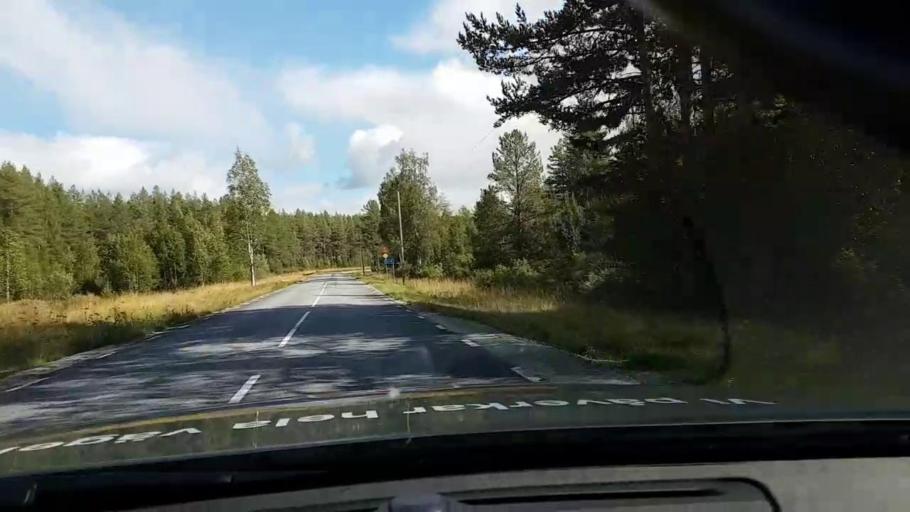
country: SE
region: Vaesterbotten
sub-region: Asele Kommun
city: Asele
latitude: 63.8604
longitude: 17.3748
